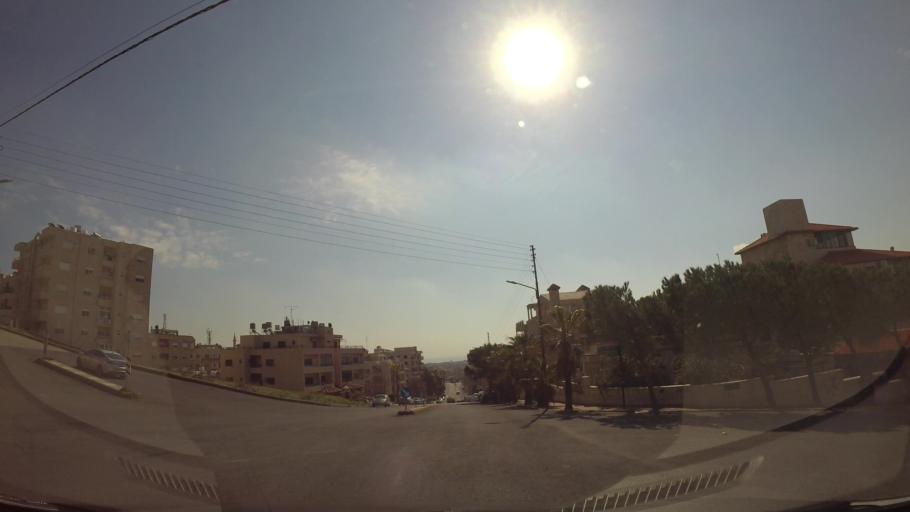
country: JO
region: Amman
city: Al Jubayhah
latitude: 31.9981
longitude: 35.8897
